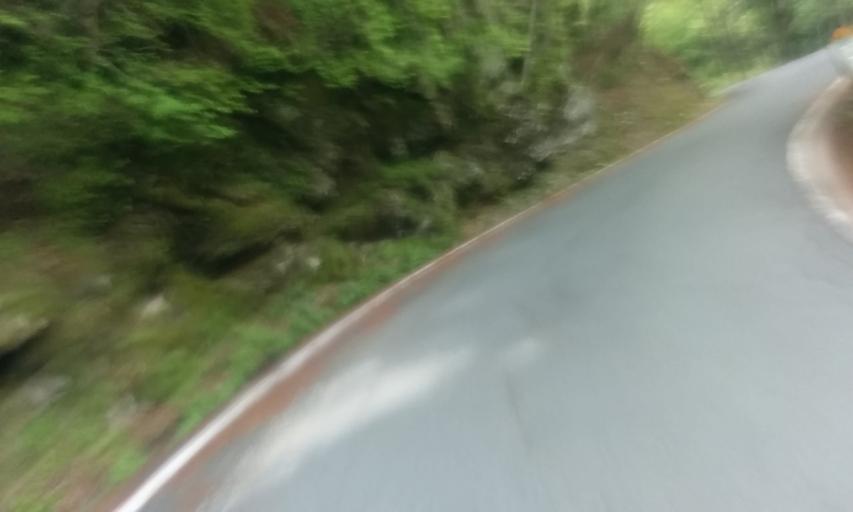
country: JP
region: Ehime
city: Saijo
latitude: 33.8007
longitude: 133.2809
